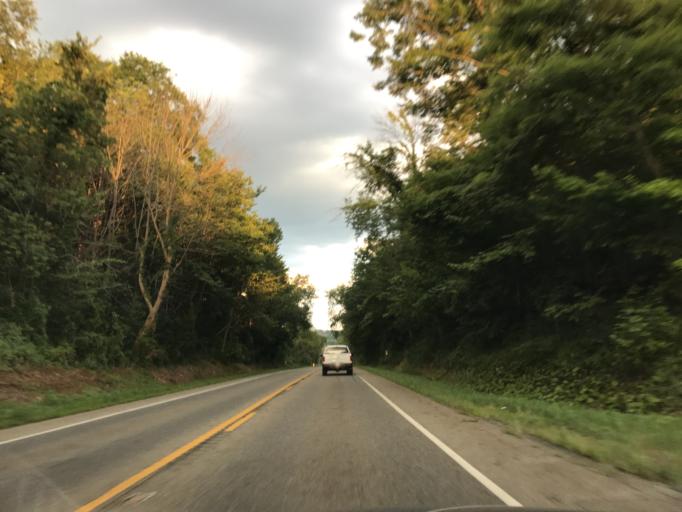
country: US
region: Ohio
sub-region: Stark County
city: East Canton
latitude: 40.7668
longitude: -81.2125
